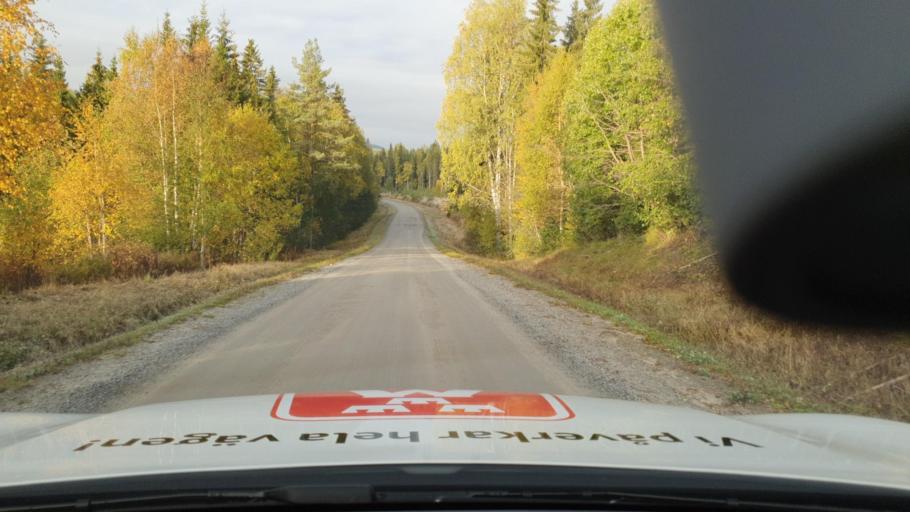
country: SE
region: Vaesterbotten
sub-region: Lycksele Kommun
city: Lycksele
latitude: 64.2159
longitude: 18.8134
